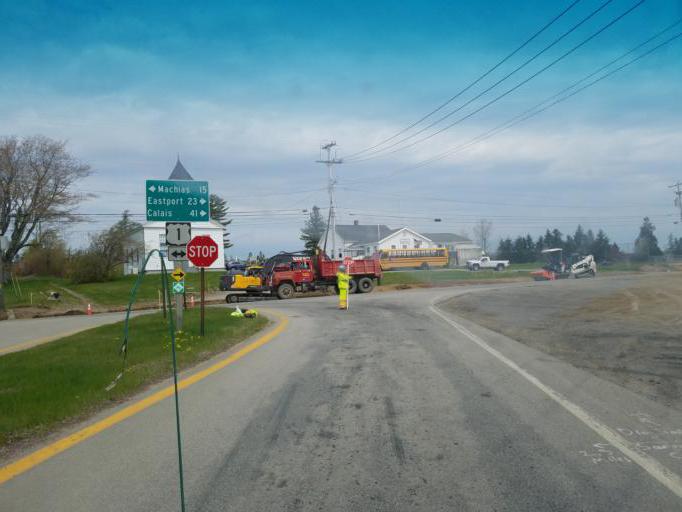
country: US
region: Maine
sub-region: Washington County
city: Eastport
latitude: 44.7906
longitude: -67.1751
